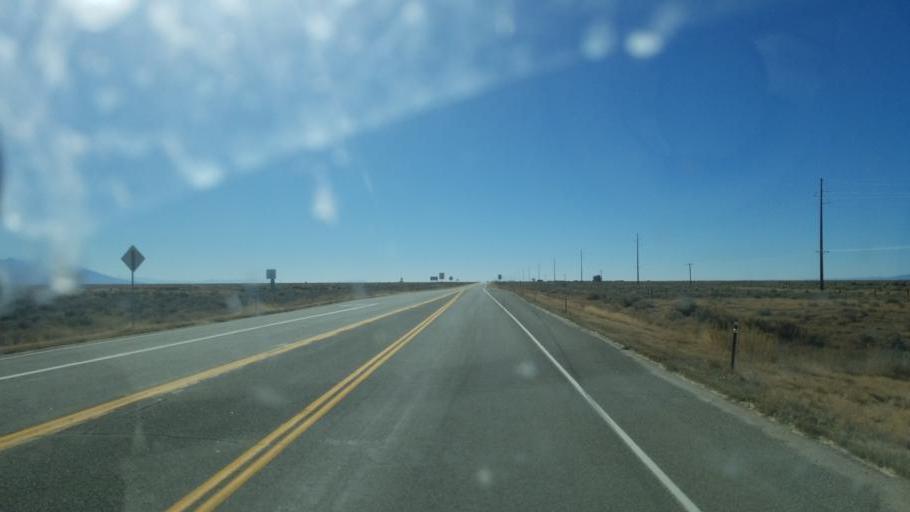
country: US
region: Colorado
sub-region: Saguache County
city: Saguache
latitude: 37.9919
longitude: -105.9078
